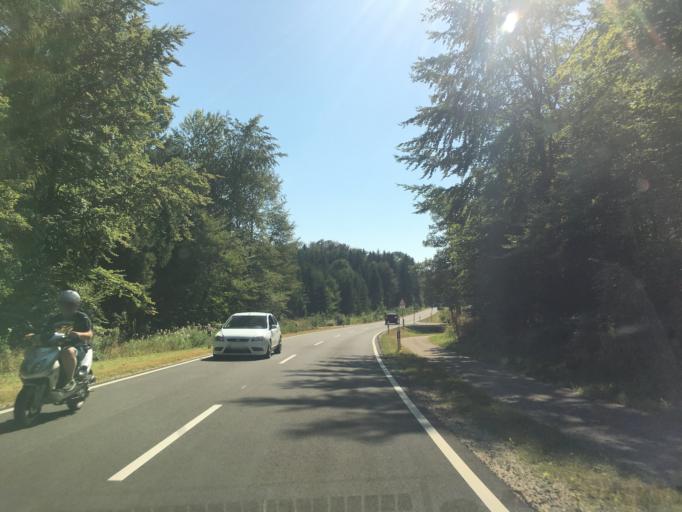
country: DE
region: Baden-Wuerttemberg
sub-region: Tuebingen Region
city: Munsingen
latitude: 48.3925
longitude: 9.4892
